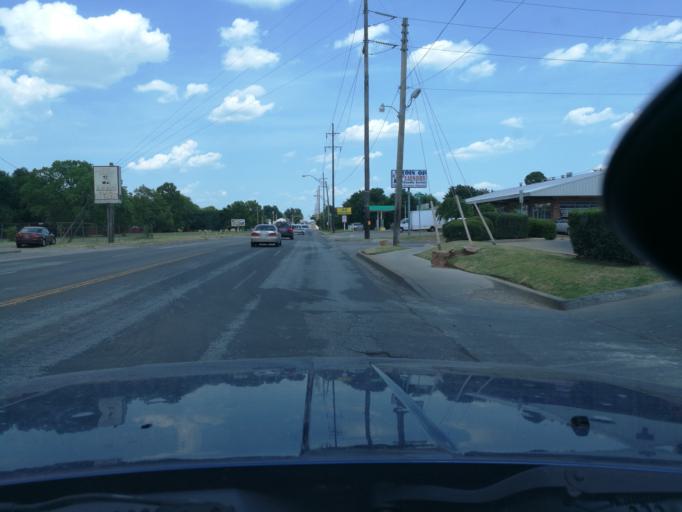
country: US
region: Oklahoma
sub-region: Oklahoma County
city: Oklahoma City
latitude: 35.4207
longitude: -97.5041
